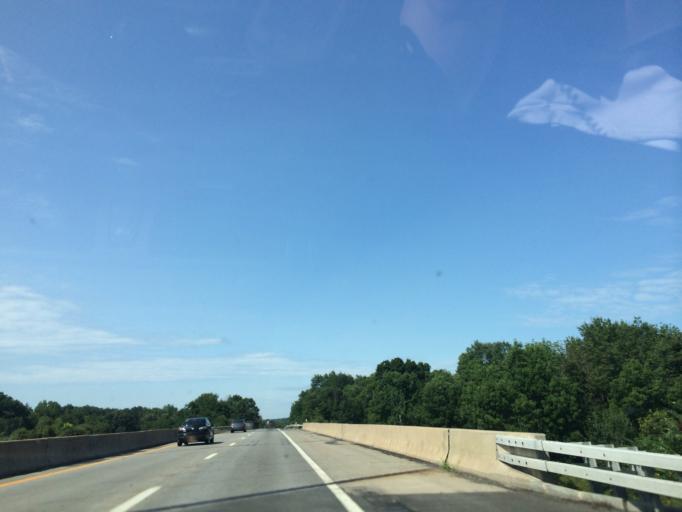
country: US
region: New York
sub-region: Orange County
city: Scotchtown
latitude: 41.4715
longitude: -74.3131
